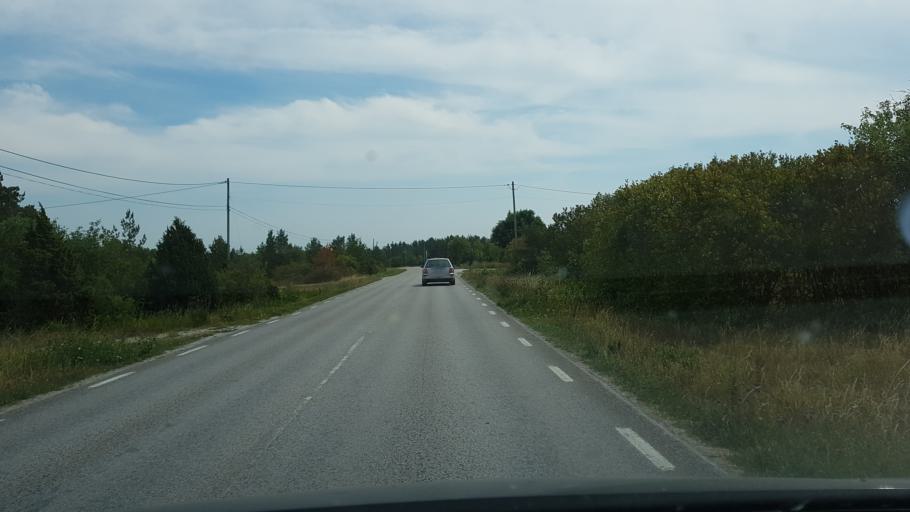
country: SE
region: Gotland
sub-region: Gotland
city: Slite
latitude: 57.7340
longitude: 18.7395
